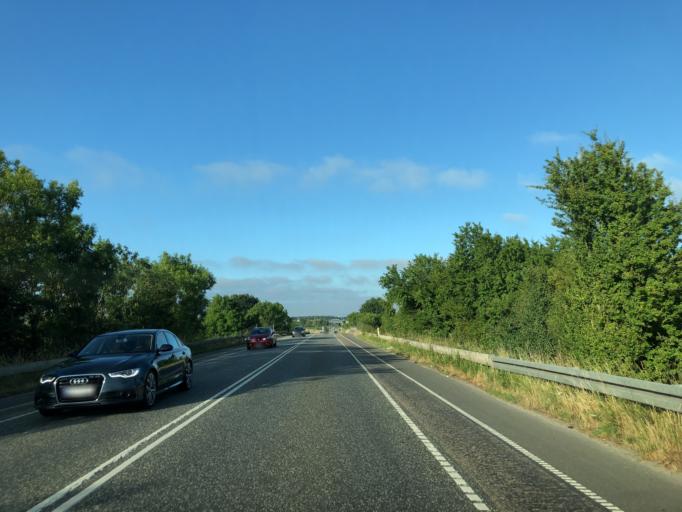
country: DK
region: South Denmark
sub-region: Fredericia Kommune
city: Taulov
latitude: 55.5498
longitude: 9.6546
